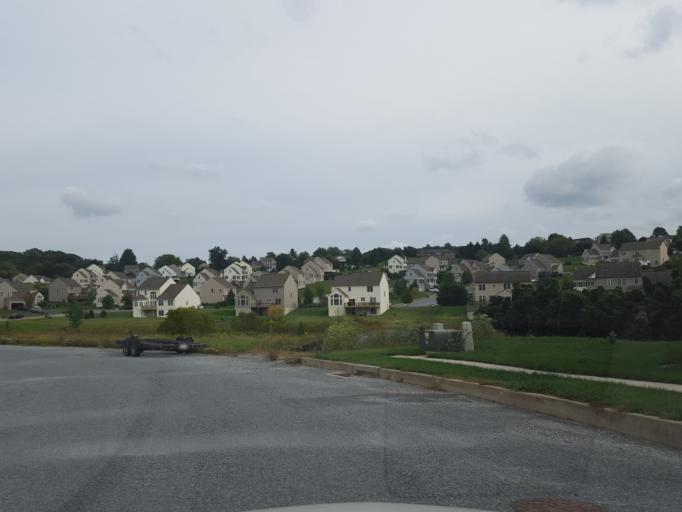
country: US
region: Pennsylvania
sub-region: York County
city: Yoe
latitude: 39.9360
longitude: -76.6530
